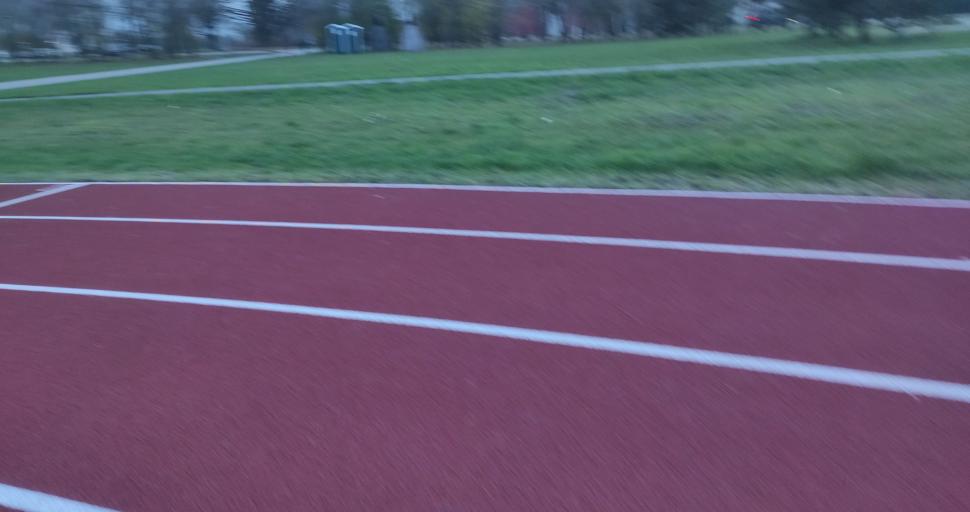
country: LV
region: Grobina
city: Grobina
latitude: 56.5381
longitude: 21.1696
